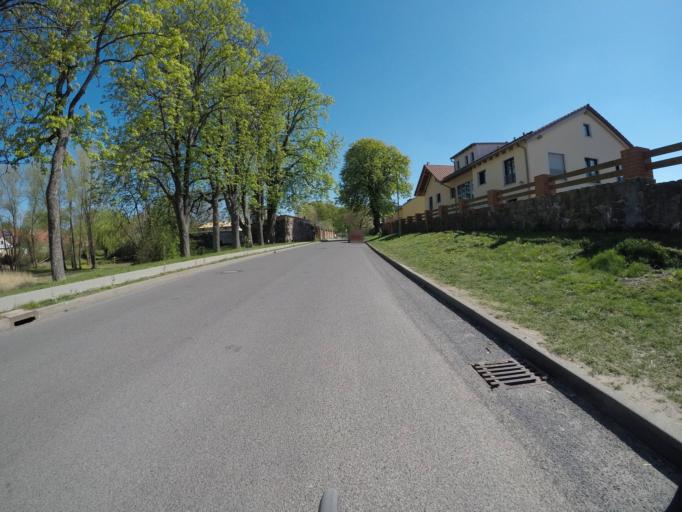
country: DE
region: Brandenburg
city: Werftpfuhl
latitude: 52.6392
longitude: 13.7944
